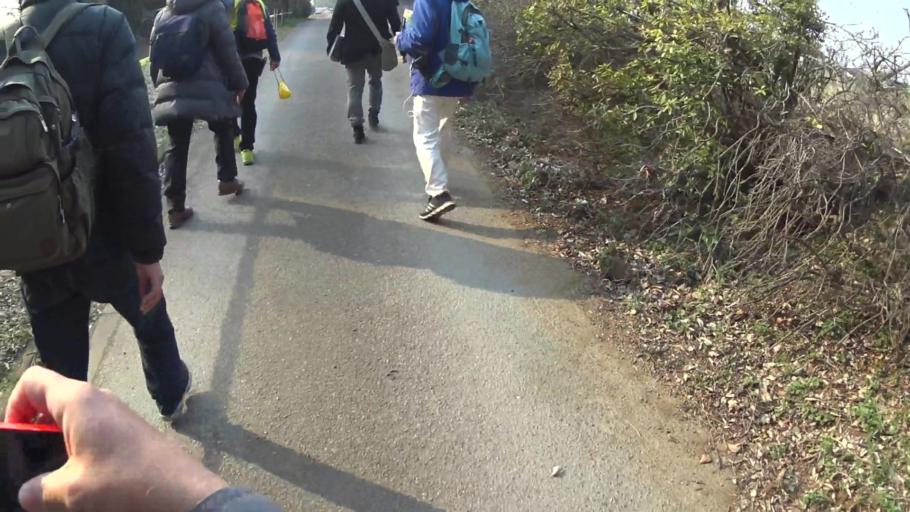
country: JP
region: Ibaraki
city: Koga
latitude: 36.1803
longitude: 139.7007
